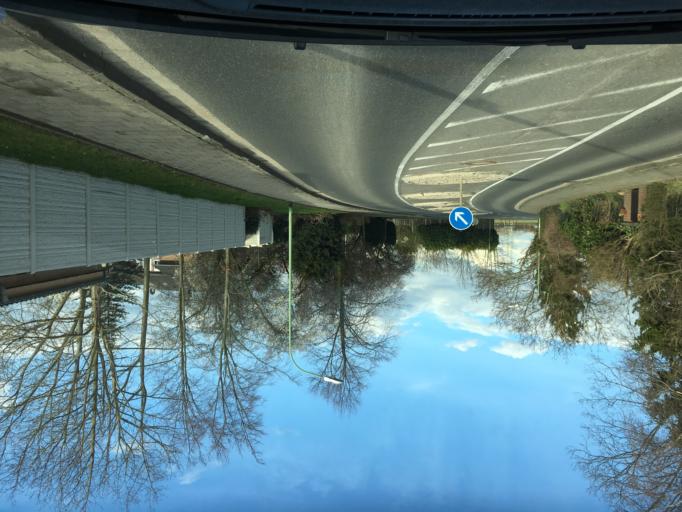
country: DE
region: North Rhine-Westphalia
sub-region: Regierungsbezirk Koln
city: Inden
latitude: 50.8276
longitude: 6.4225
